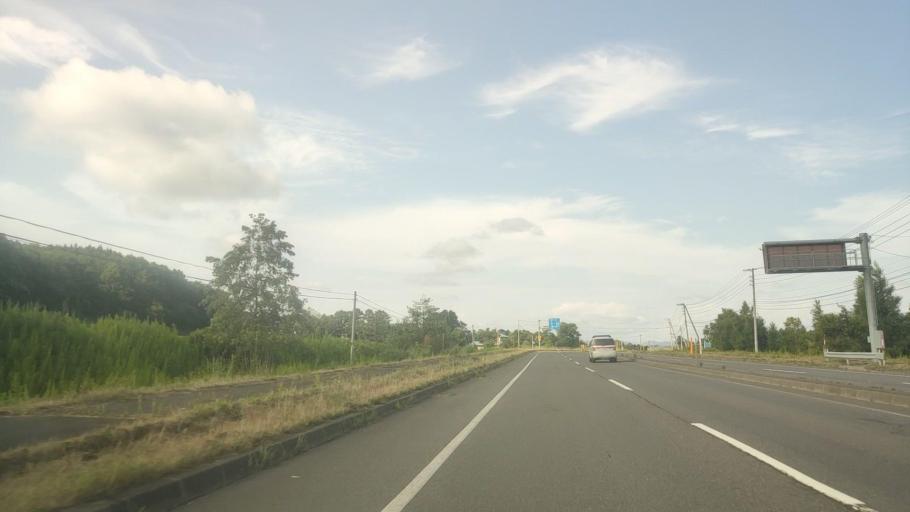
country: JP
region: Hokkaido
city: Chitose
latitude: 42.7738
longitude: 141.8267
